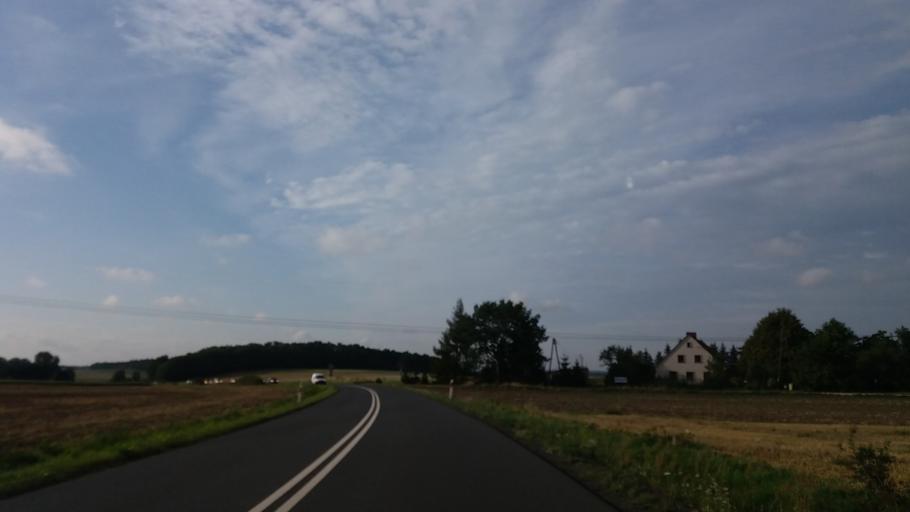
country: PL
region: Lower Silesian Voivodeship
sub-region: Powiat legnicki
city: Legnickie Pole
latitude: 51.1553
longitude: 16.3438
